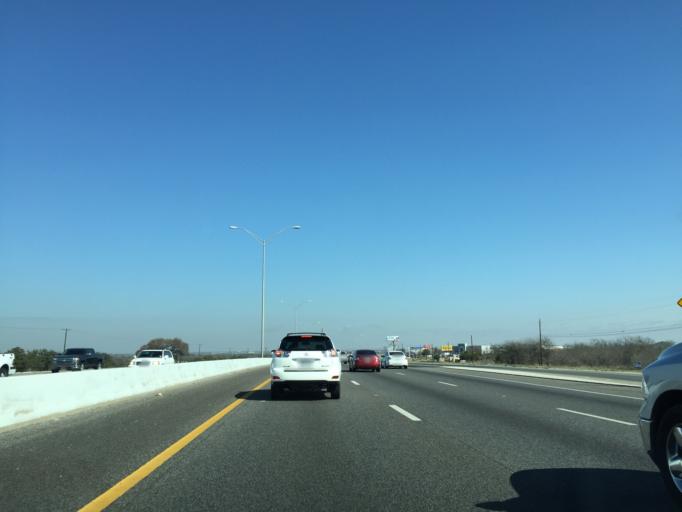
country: US
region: Texas
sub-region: Williamson County
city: Georgetown
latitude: 30.5880
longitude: -97.6923
